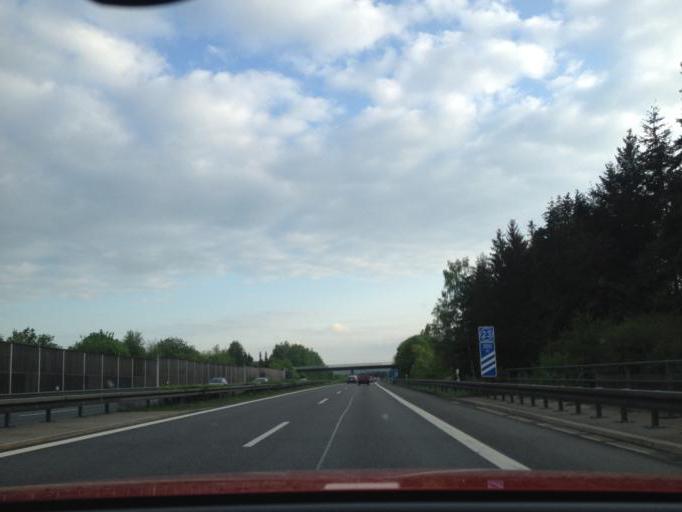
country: DE
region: Bavaria
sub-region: Upper Palatinate
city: Weiden
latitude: 49.6908
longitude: 12.1315
